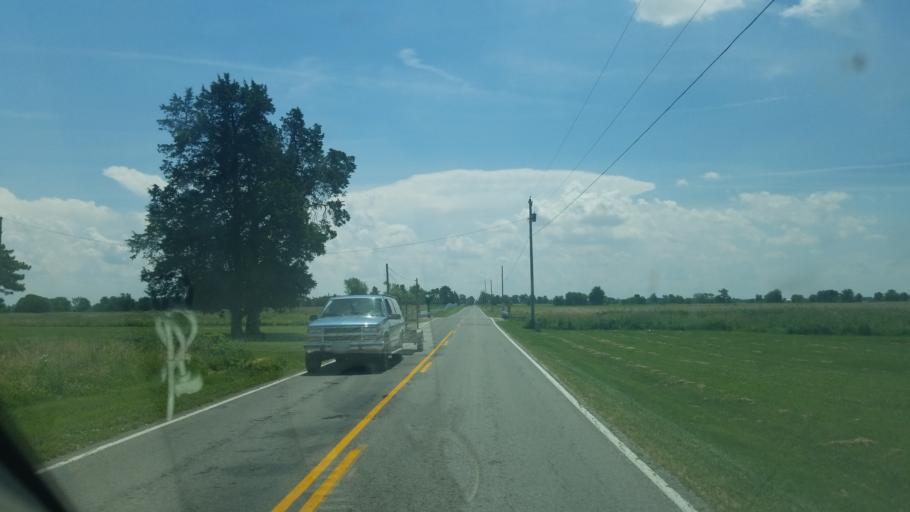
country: US
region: Ohio
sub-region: Hancock County
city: Arlington
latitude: 40.9476
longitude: -83.5943
